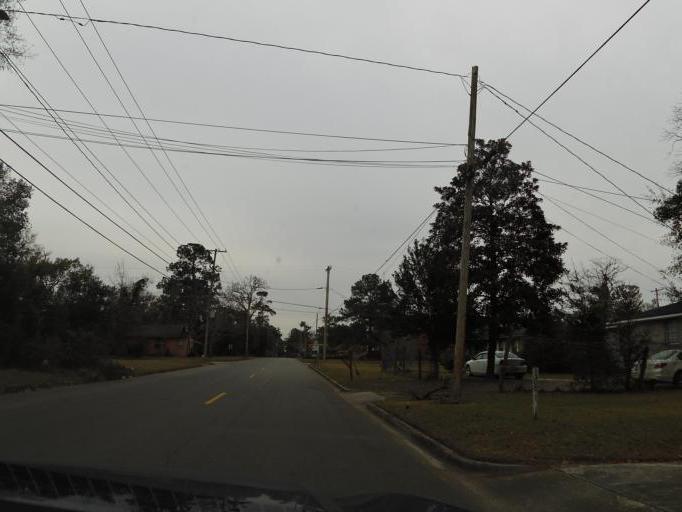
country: US
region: Georgia
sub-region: Thomas County
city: Thomasville
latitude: 30.8166
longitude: -83.9796
